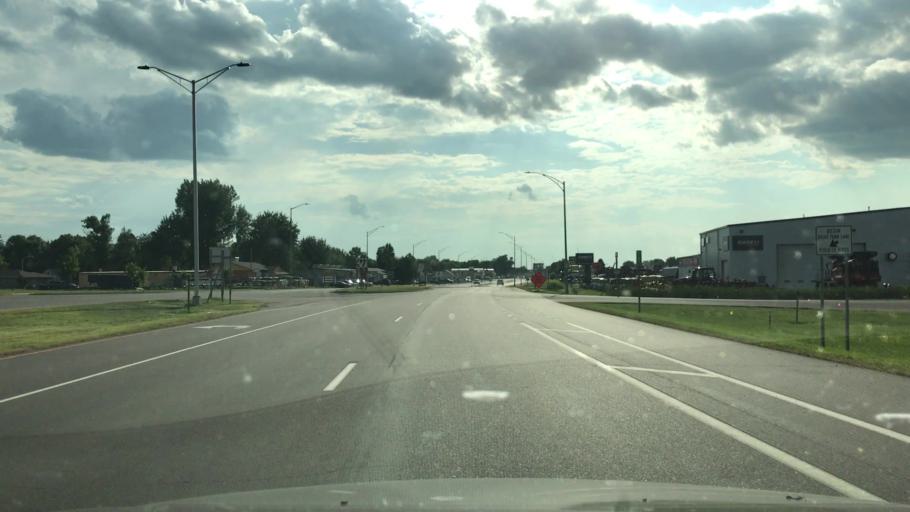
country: US
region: Minnesota
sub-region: Nobles County
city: Worthington
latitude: 43.6312
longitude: -95.5793
